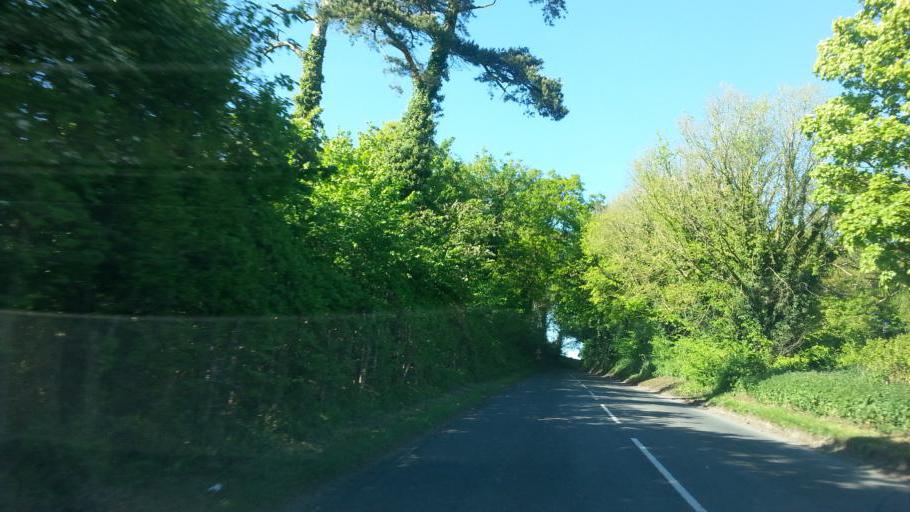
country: GB
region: England
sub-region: Somerset
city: Milborne Port
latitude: 50.9683
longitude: -2.4260
